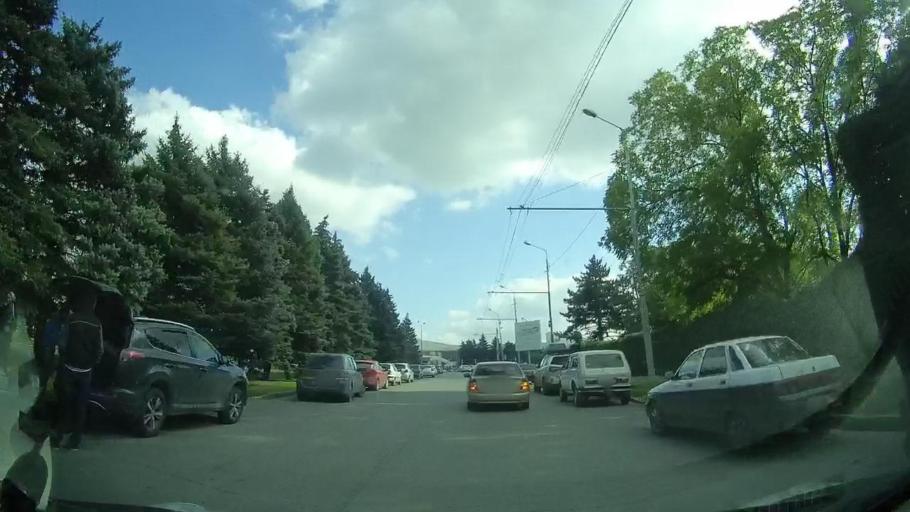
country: RU
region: Rostov
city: Imeni Chkalova
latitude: 47.2560
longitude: 39.8014
